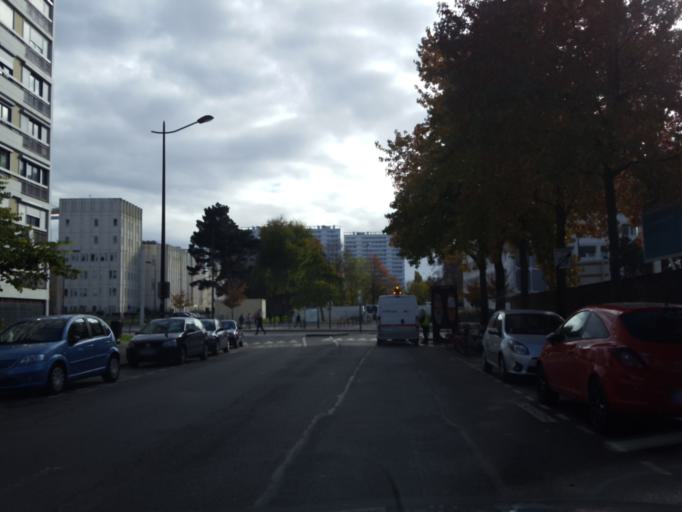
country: FR
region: Pays de la Loire
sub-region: Departement de la Loire-Atlantique
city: Nantes
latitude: 47.2072
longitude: -1.5419
